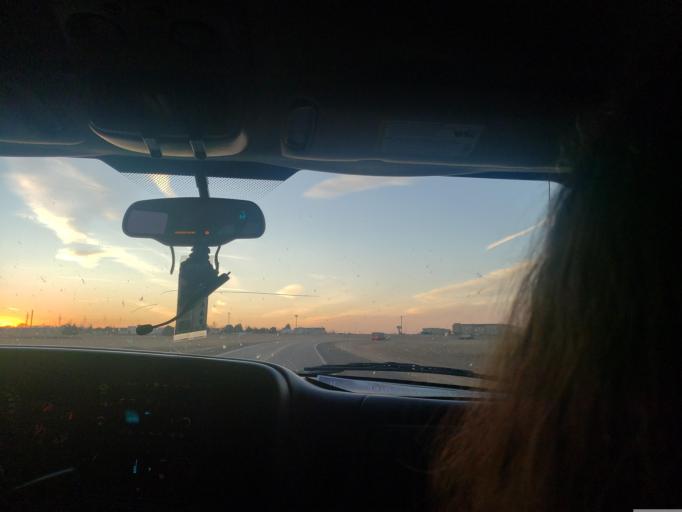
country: US
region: Kansas
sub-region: Seward County
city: Liberal
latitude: 37.0705
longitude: -100.9150
